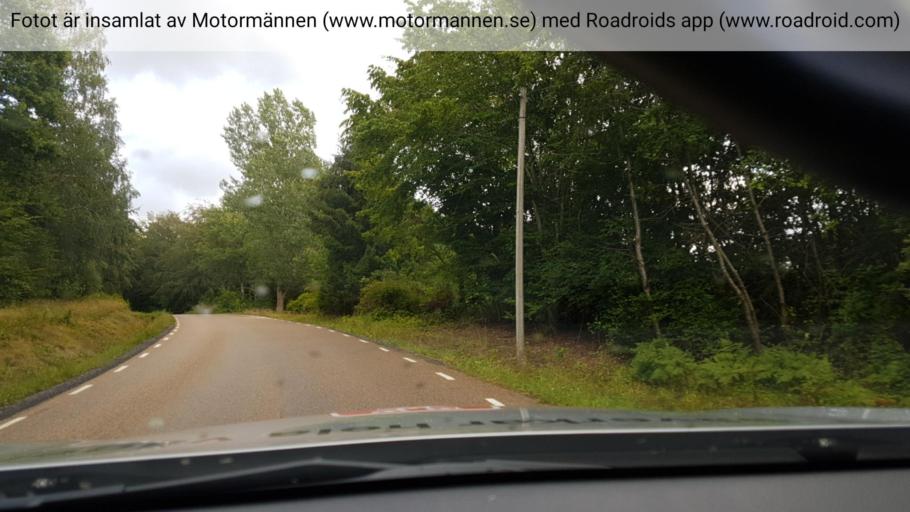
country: SE
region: Vaestra Goetaland
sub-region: Uddevalla Kommun
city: Uddevalla
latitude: 58.3178
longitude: 11.8615
